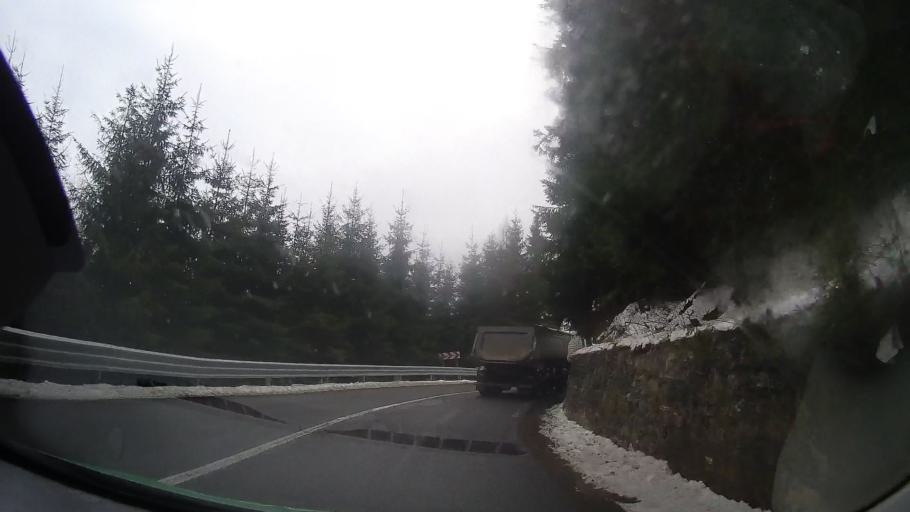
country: RO
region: Neamt
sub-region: Comuna Bicaz Chei
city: Bicaz Chei
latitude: 46.7809
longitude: 25.7490
